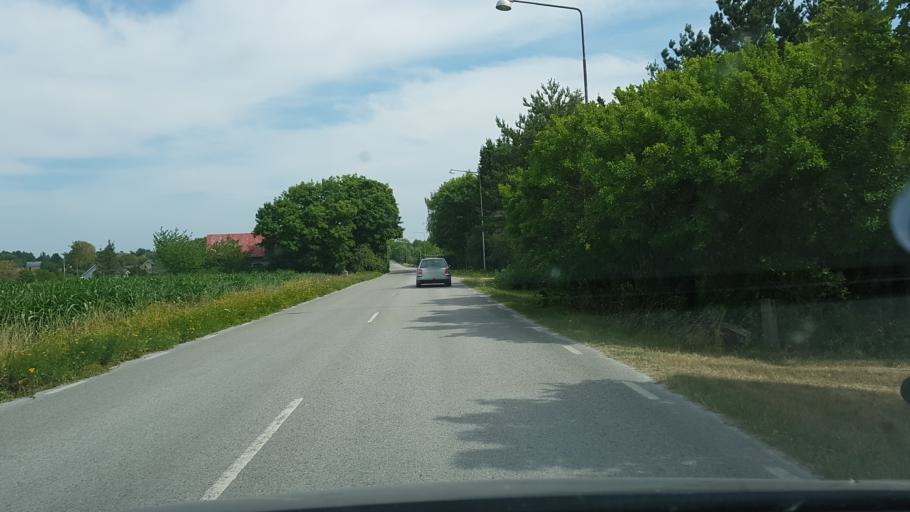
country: SE
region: Gotland
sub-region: Gotland
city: Slite
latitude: 57.7218
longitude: 18.7805
